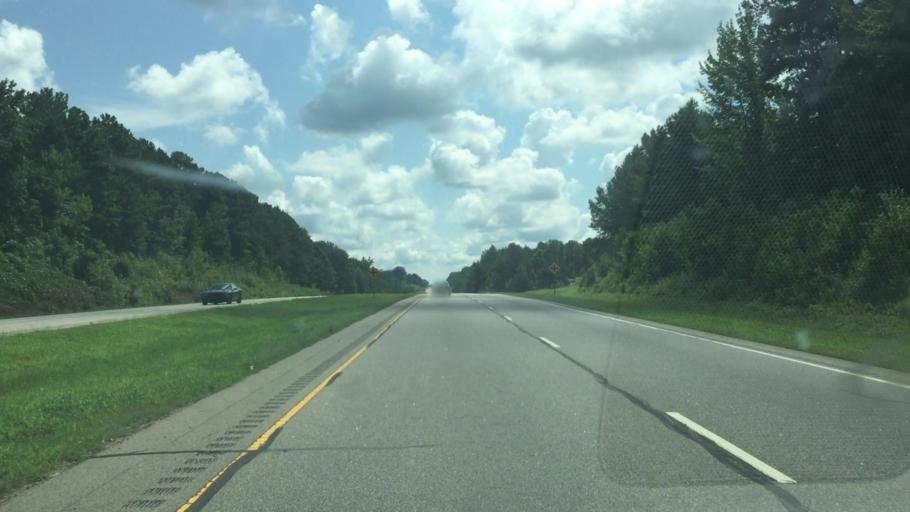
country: US
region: North Carolina
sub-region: Anson County
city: Wadesboro
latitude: 34.9632
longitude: -80.0128
